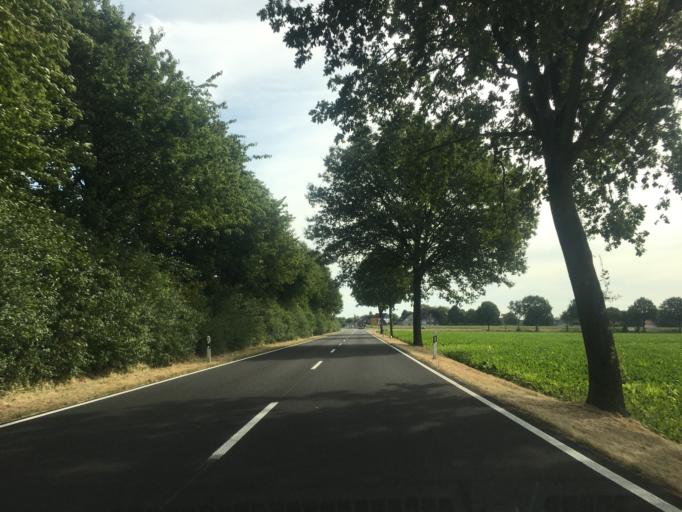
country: DE
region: North Rhine-Westphalia
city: Erkelenz
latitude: 51.0804
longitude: 6.2750
